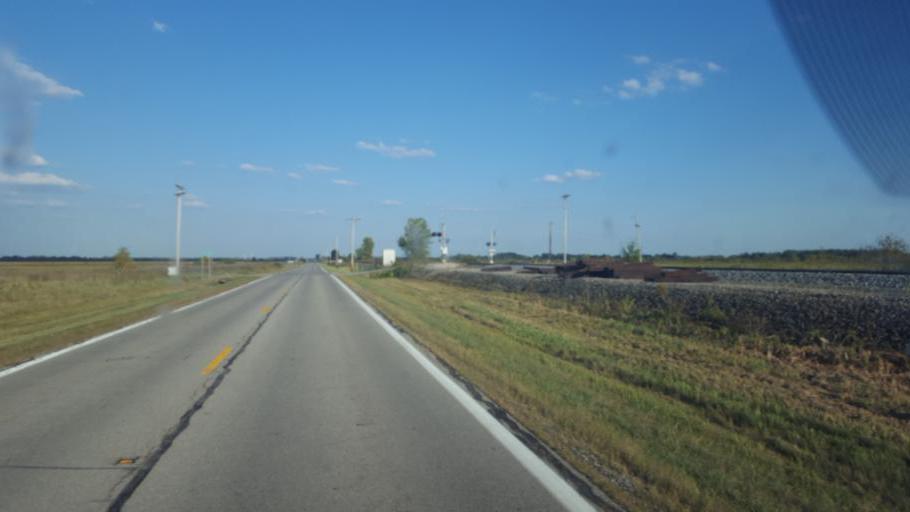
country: US
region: Ohio
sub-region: Marion County
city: Marion
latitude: 40.5861
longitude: -83.2568
